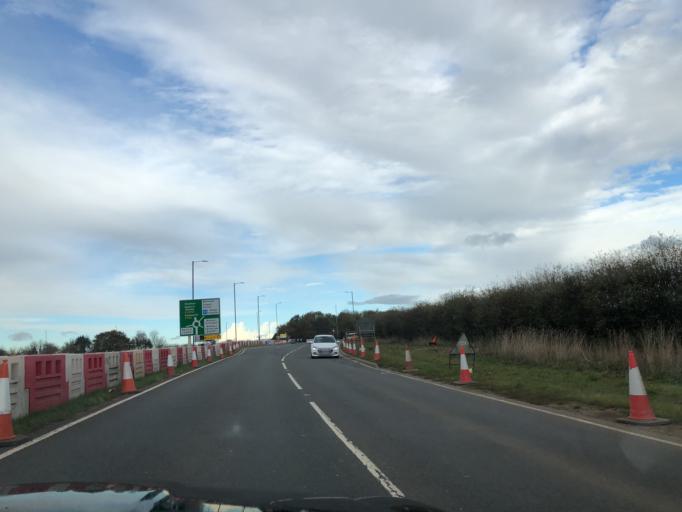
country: GB
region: England
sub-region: Warwickshire
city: Warwick
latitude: 52.2679
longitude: -1.5602
